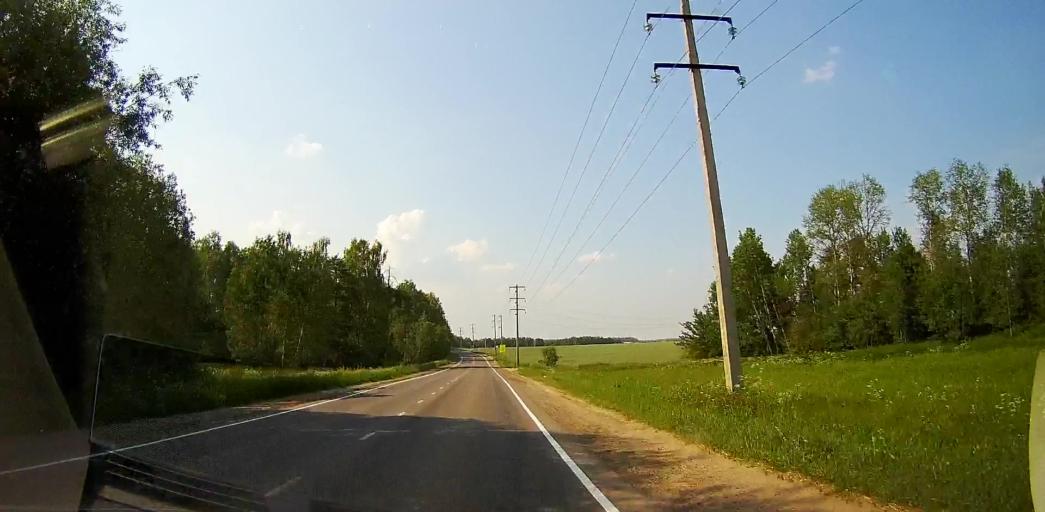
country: RU
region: Moskovskaya
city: Barybino
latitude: 55.2840
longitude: 37.9158
